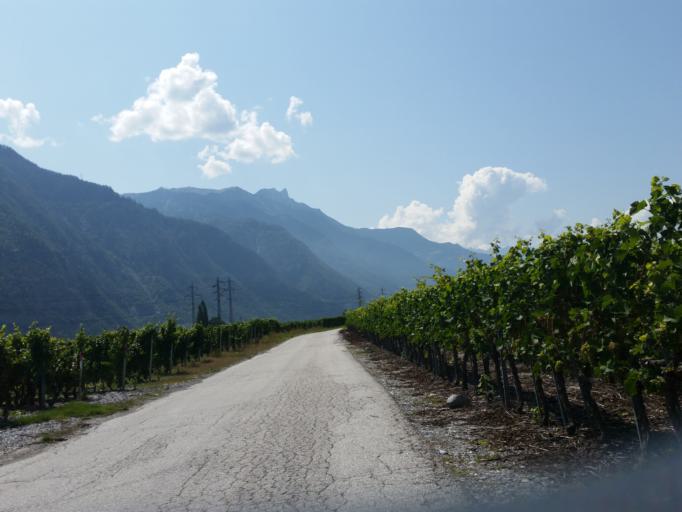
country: CH
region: Valais
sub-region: Conthey District
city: Ardon
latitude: 46.1998
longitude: 7.2527
